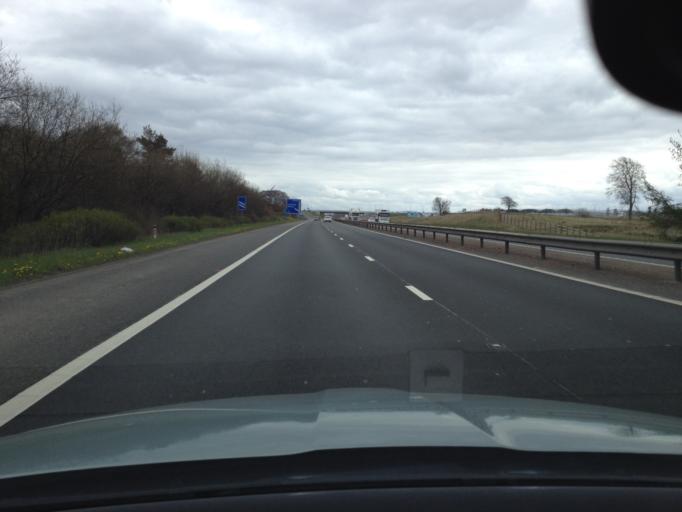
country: GB
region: Scotland
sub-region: West Lothian
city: Armadale
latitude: 55.8702
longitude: -3.7142
